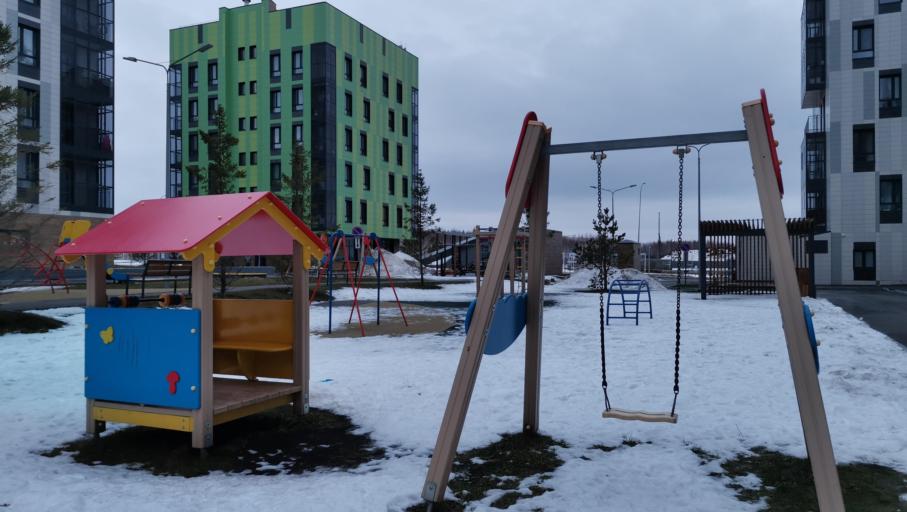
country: RU
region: Tatarstan
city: Sviyazhsk
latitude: 55.7479
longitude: 48.7420
